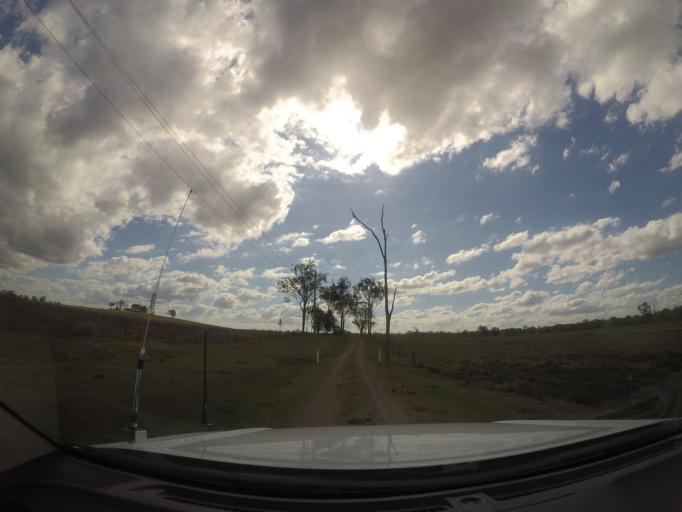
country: AU
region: Queensland
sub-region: Logan
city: North Maclean
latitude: -27.8089
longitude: 153.0048
